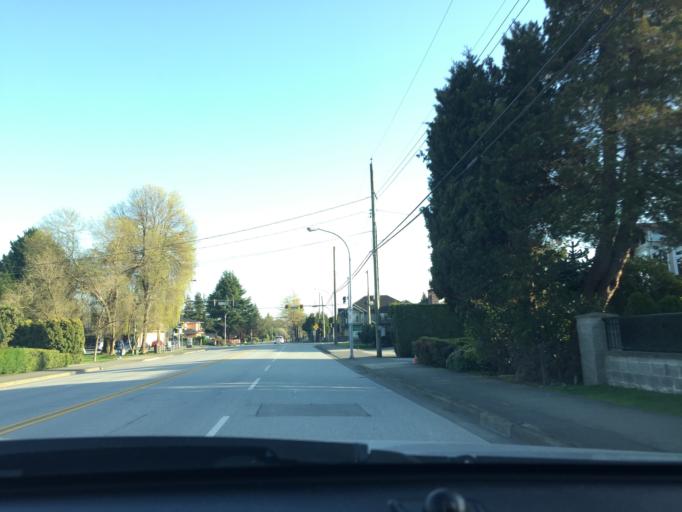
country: CA
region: British Columbia
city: Richmond
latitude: 49.1492
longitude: -123.1253
